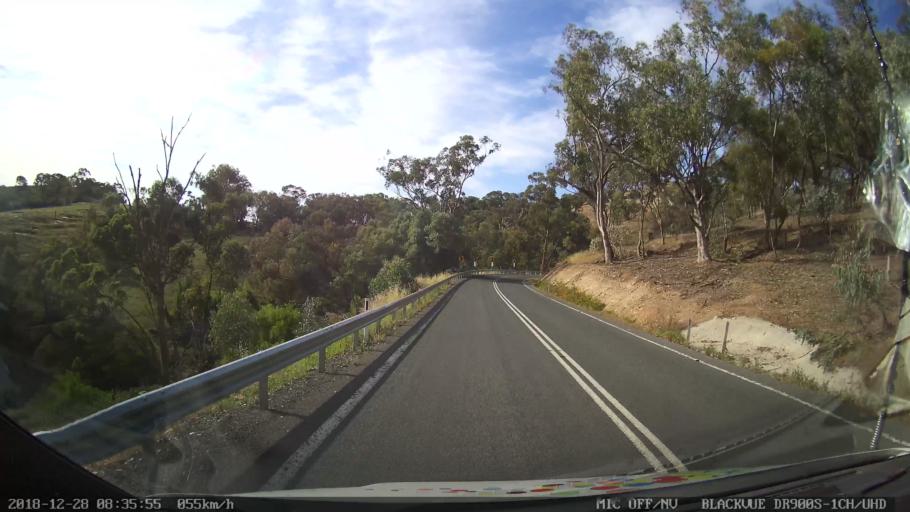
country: AU
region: New South Wales
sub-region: Blayney
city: Blayney
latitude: -33.9863
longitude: 149.3106
